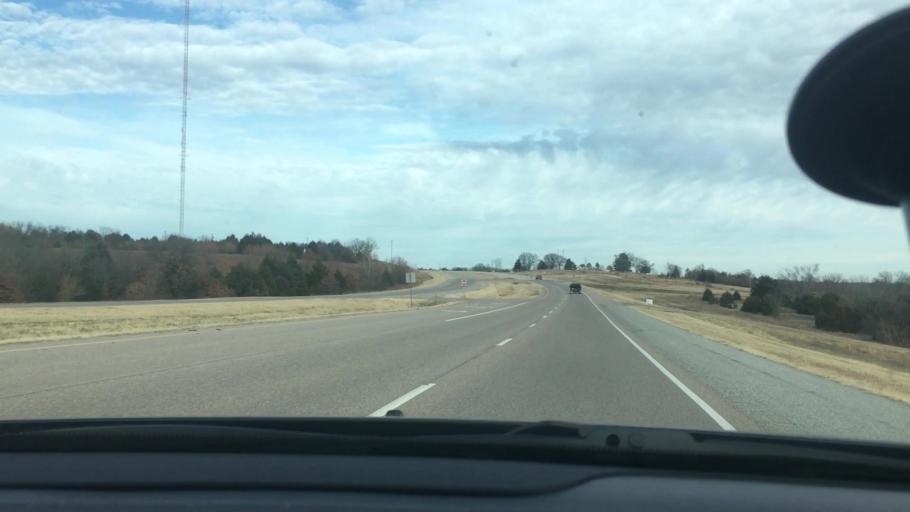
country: US
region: Oklahoma
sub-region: Pontotoc County
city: Byng
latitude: 34.8966
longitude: -96.6748
